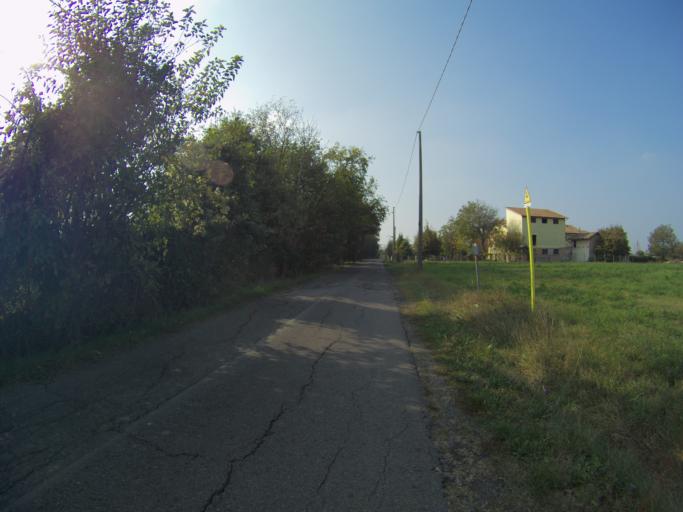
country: IT
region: Emilia-Romagna
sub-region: Provincia di Reggio Emilia
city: Forche
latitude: 44.6540
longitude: 10.5610
